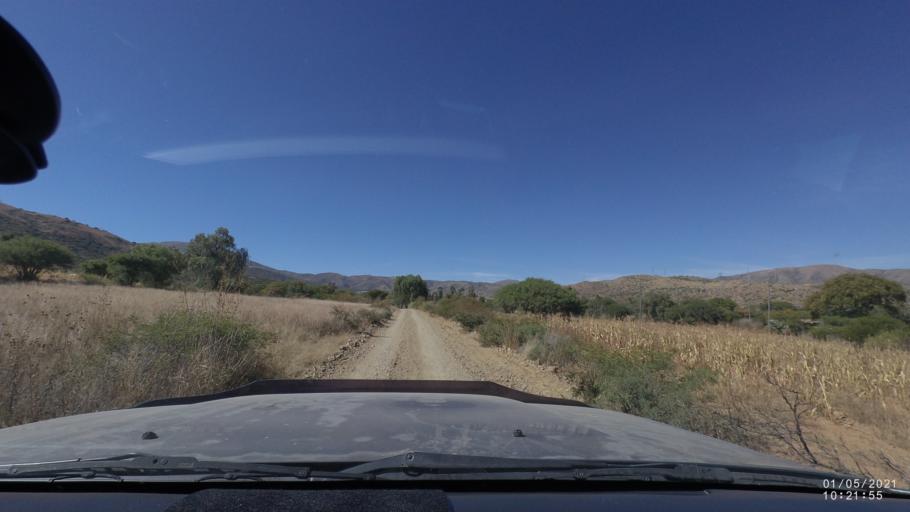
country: BO
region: Cochabamba
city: Capinota
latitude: -17.5667
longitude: -66.2007
